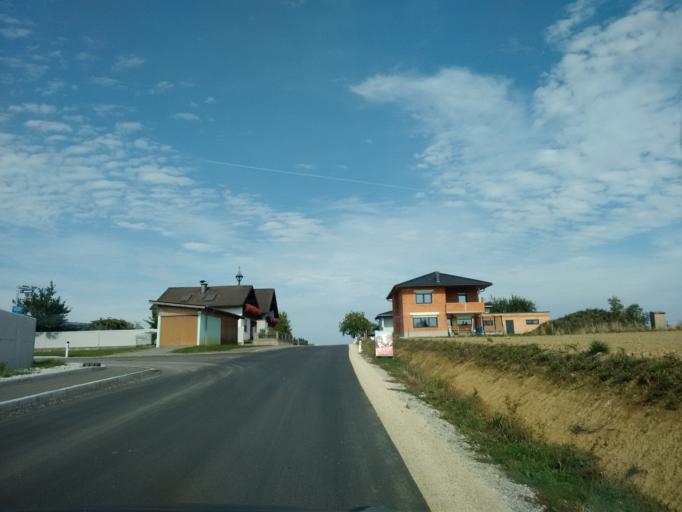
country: AT
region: Upper Austria
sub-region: Wels-Land
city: Marchtrenk
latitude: 48.1244
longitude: 14.0979
